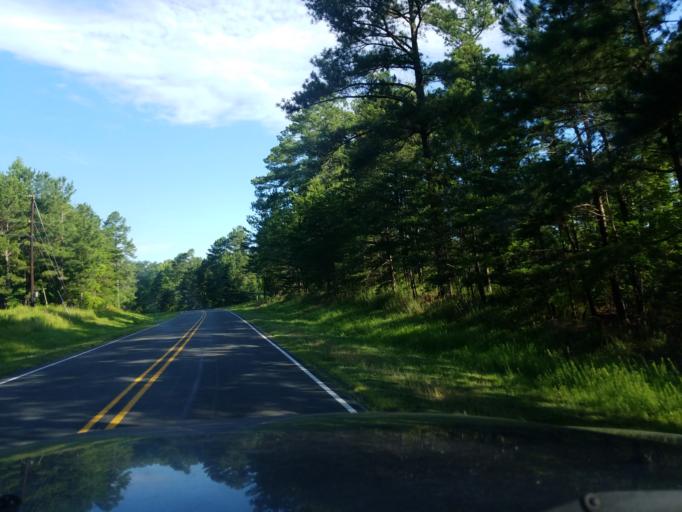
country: US
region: North Carolina
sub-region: Granville County
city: Butner
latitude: 36.1818
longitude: -78.8067
